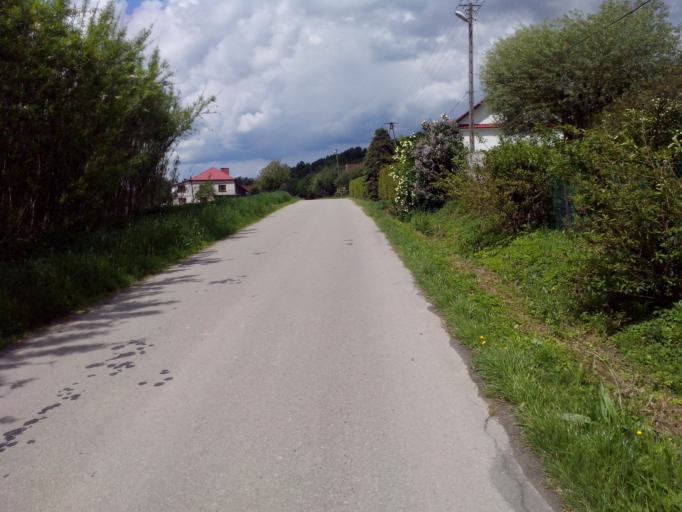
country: PL
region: Subcarpathian Voivodeship
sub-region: Powiat strzyzowski
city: Strzyzow
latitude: 49.8479
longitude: 21.8172
